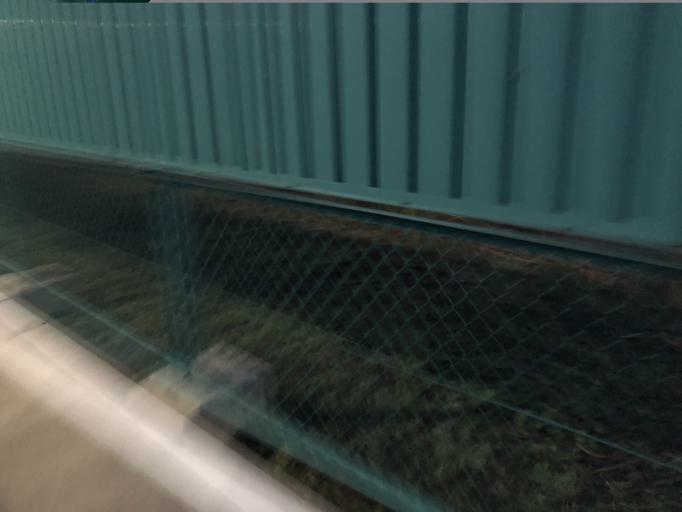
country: JP
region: Kanagawa
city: Atsugi
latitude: 35.4602
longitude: 139.3685
